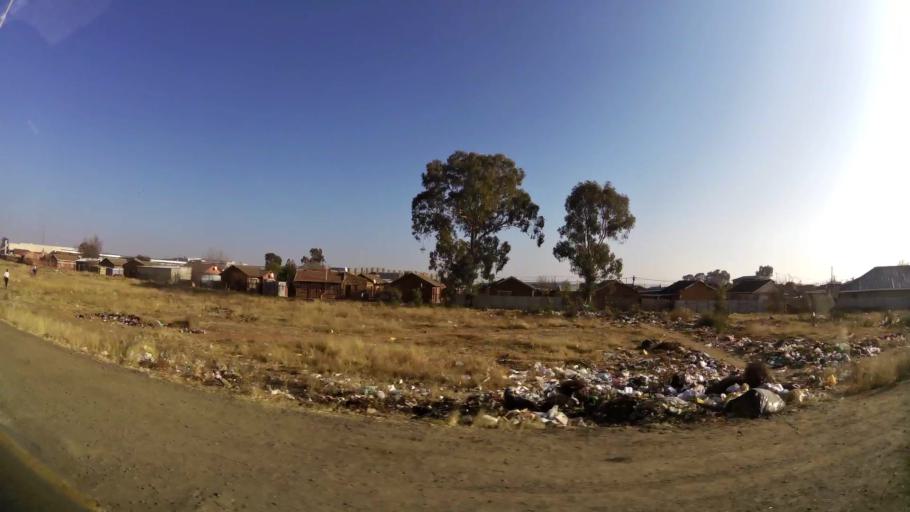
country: ZA
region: Orange Free State
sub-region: Mangaung Metropolitan Municipality
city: Bloemfontein
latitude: -29.1597
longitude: 26.2591
